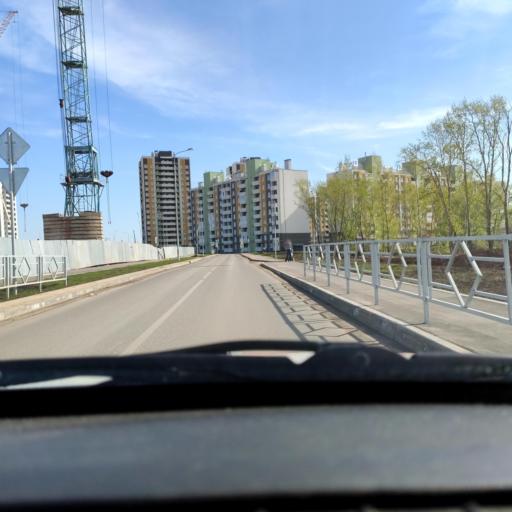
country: RU
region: Samara
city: Samara
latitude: 53.1013
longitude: 50.1706
